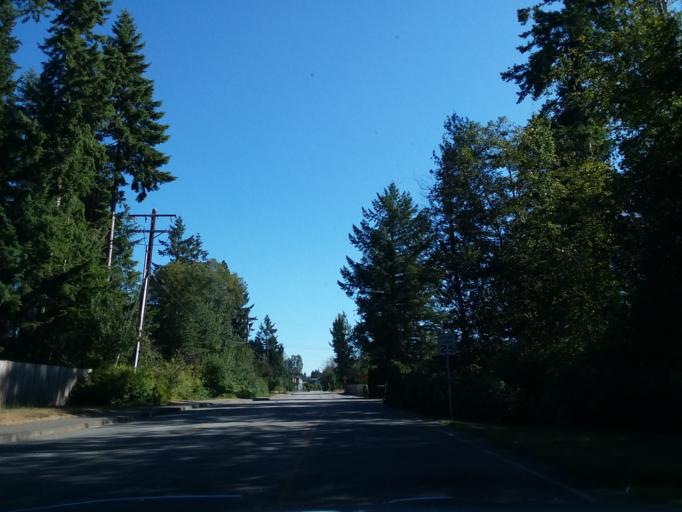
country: US
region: Washington
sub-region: Snohomish County
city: Smokey Point
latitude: 48.1598
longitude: -122.1966
